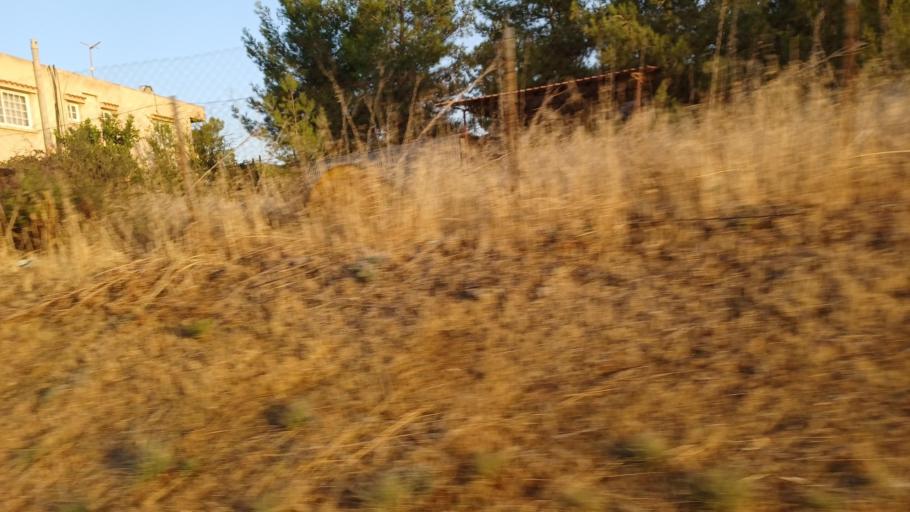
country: CY
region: Lefkosia
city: Lythrodontas
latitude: 34.9481
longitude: 33.2904
